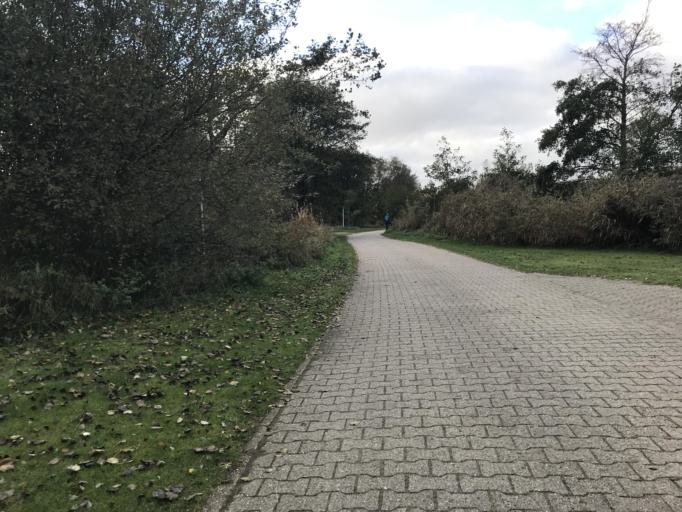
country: DE
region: Lower Saxony
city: Borkum
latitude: 53.6027
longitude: 6.7269
